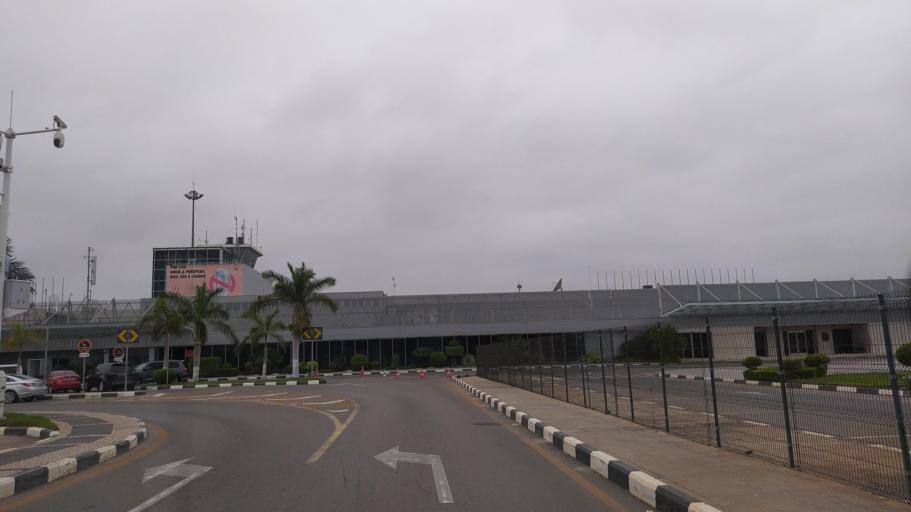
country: AO
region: Luanda
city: Luanda
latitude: -8.8477
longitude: 13.2341
